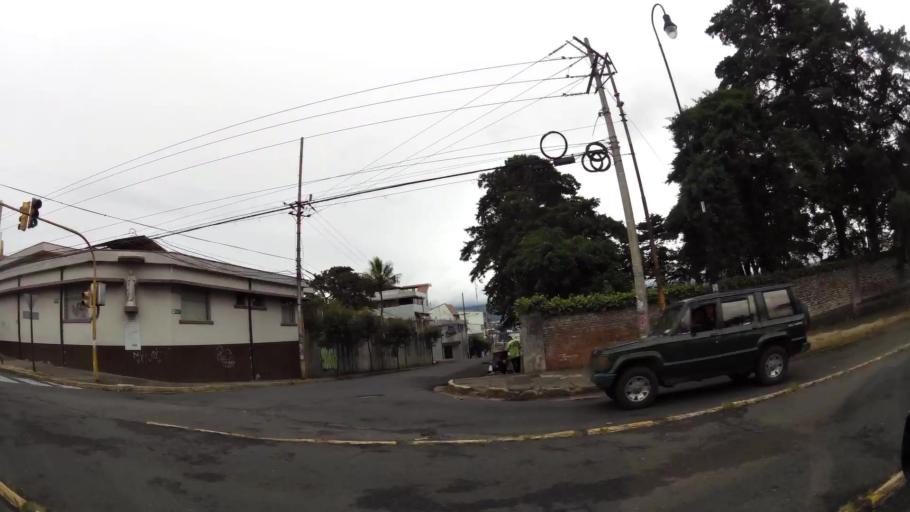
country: CR
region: San Jose
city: San Jose
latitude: 9.9297
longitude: -84.0885
